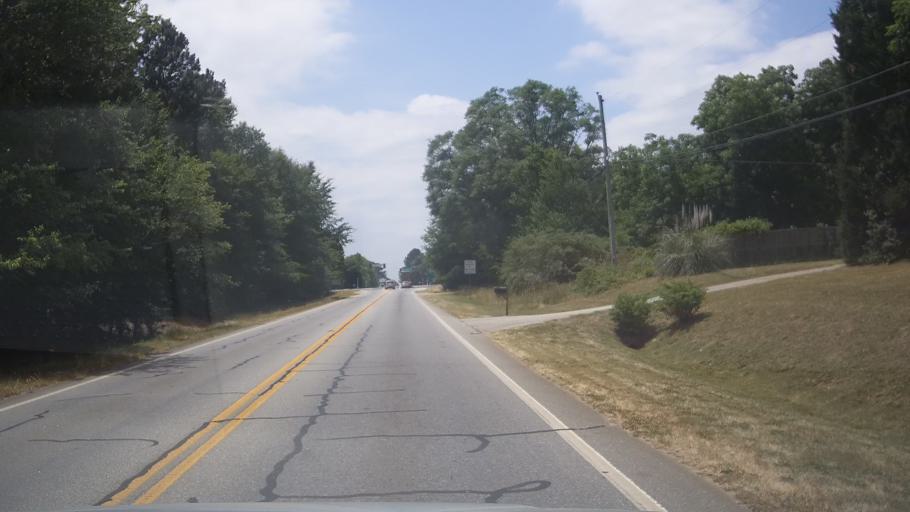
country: US
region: Georgia
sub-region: Jackson County
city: Commerce
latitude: 34.1938
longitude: -83.4290
